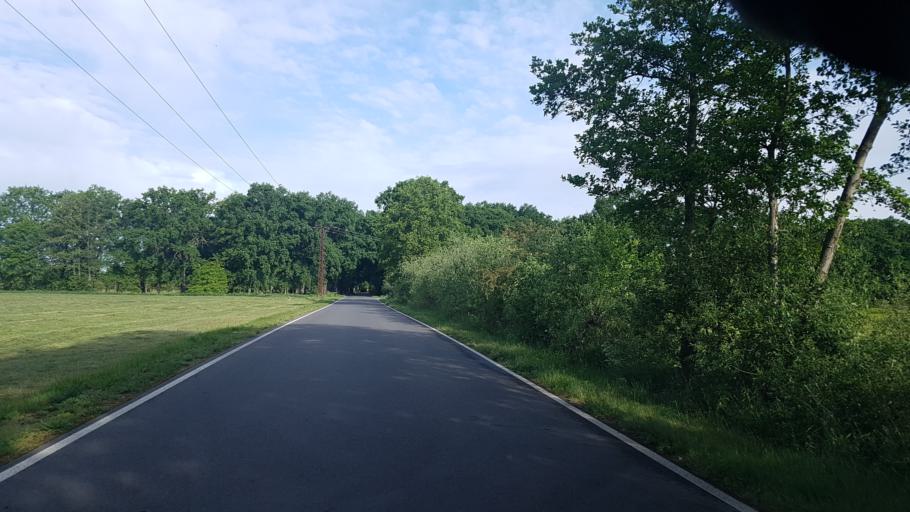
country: DE
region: Brandenburg
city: Luckau
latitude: 51.8276
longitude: 13.7503
